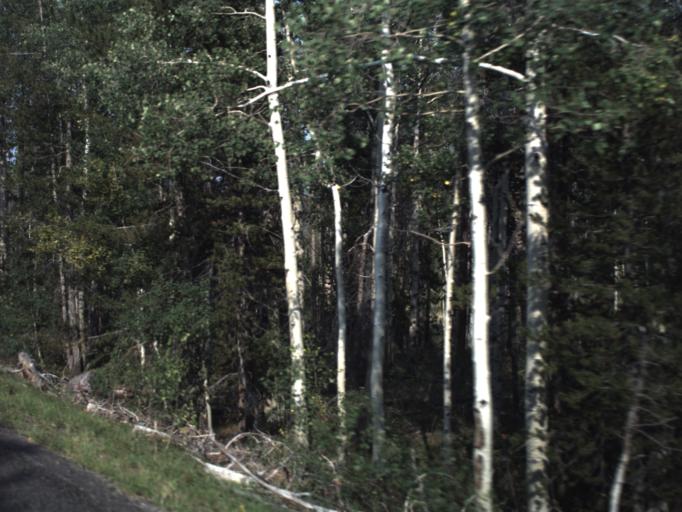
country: US
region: Utah
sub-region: Summit County
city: Oakley
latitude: 40.7997
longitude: -110.8821
